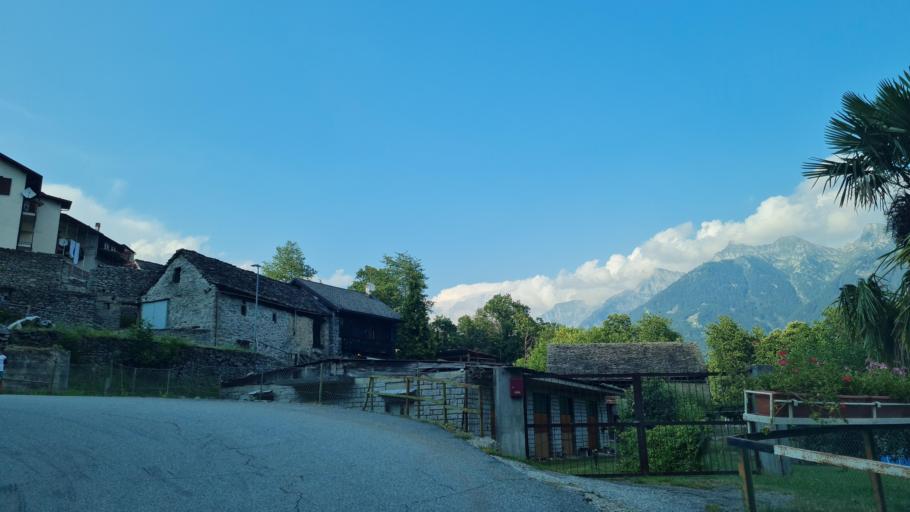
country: IT
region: Piedmont
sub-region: Provincia Verbano-Cusio-Ossola
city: Crodo
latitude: 46.2206
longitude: 8.3079
